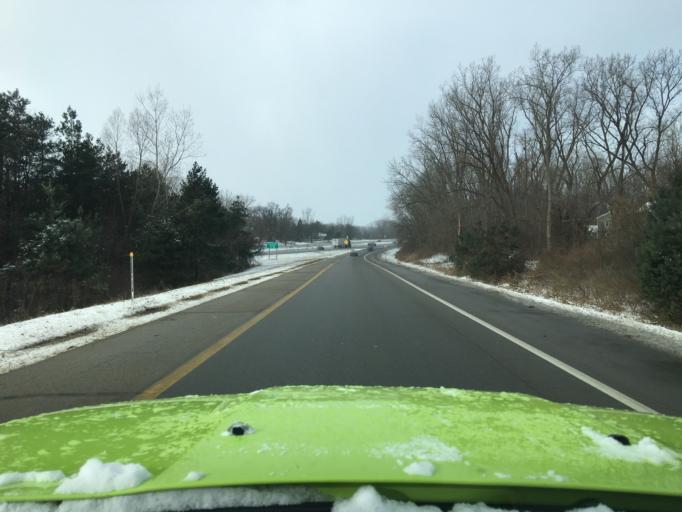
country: US
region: Michigan
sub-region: Kent County
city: East Grand Rapids
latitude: 42.9633
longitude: -85.5784
